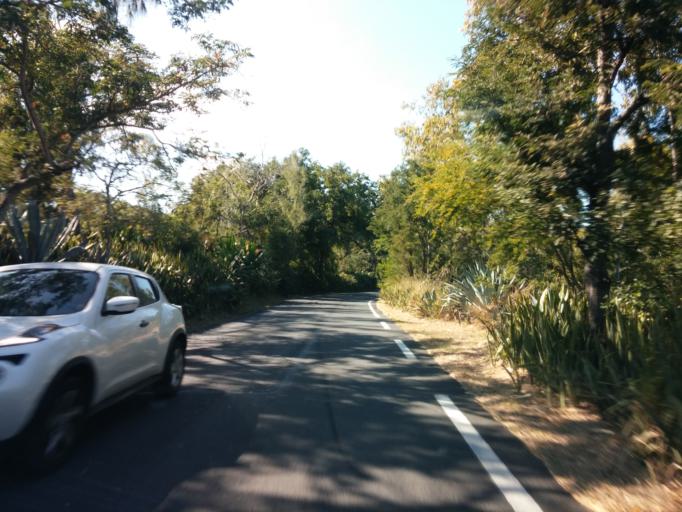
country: RE
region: Reunion
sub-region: Reunion
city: Les Avirons
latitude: -21.2609
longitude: 55.3518
